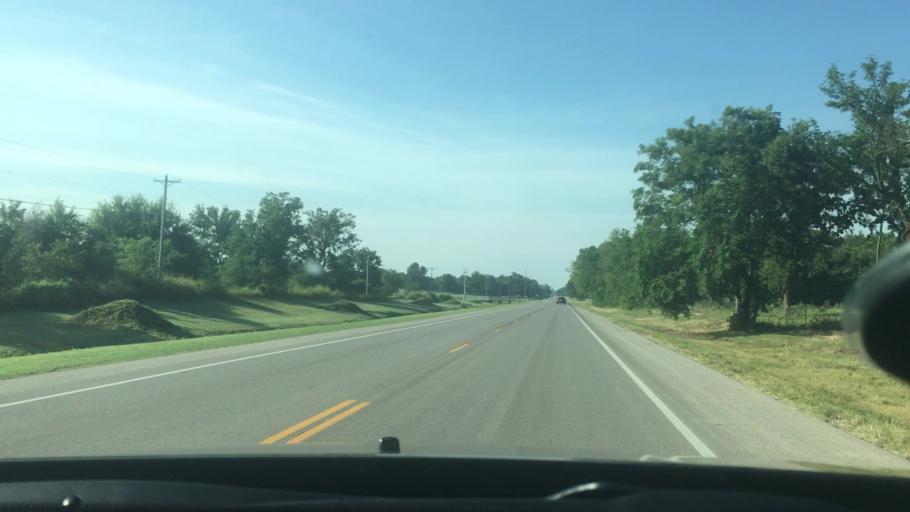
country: US
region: Oklahoma
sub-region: Garvin County
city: Pauls Valley
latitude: 34.6983
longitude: -97.2129
